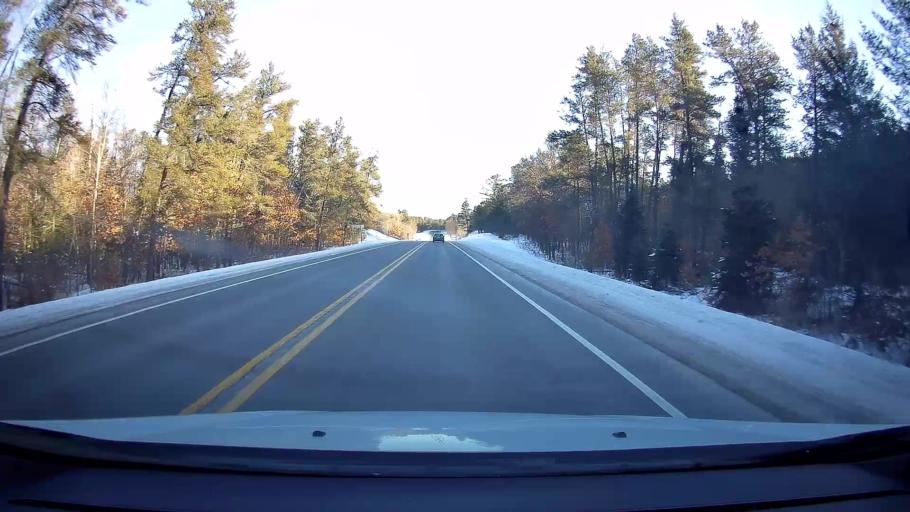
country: US
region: Wisconsin
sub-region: Sawyer County
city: Hayward
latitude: 45.9543
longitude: -91.6828
